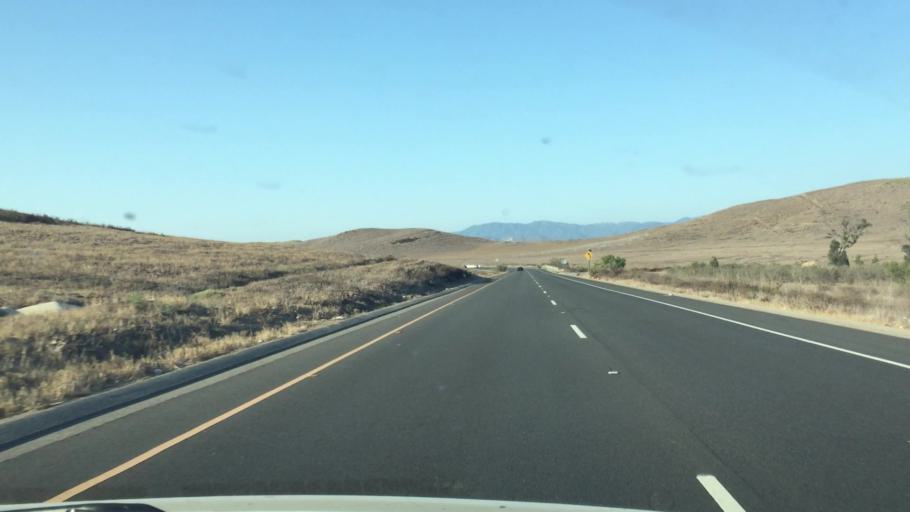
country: US
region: California
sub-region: Orange County
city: Laguna Woods
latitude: 33.6169
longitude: -117.7585
